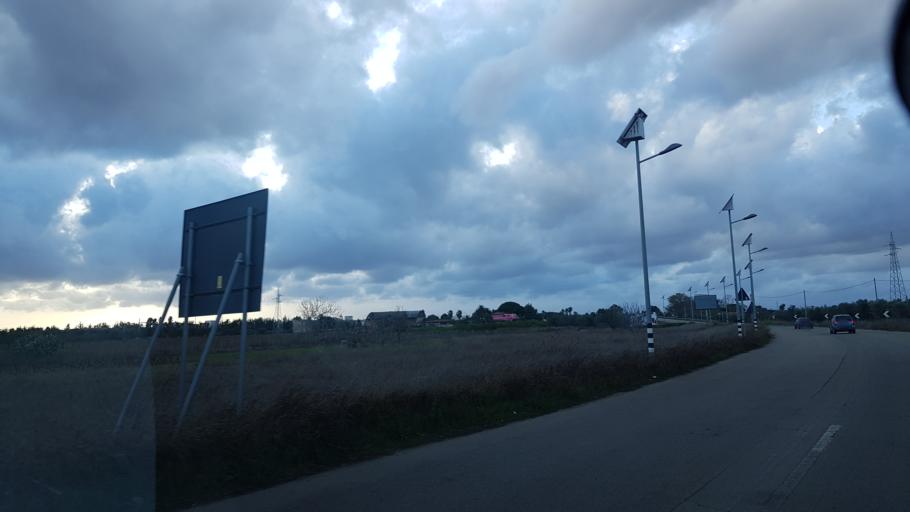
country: IT
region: Apulia
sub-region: Provincia di Brindisi
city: San Pietro Vernotico
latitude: 40.4998
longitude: 18.0028
